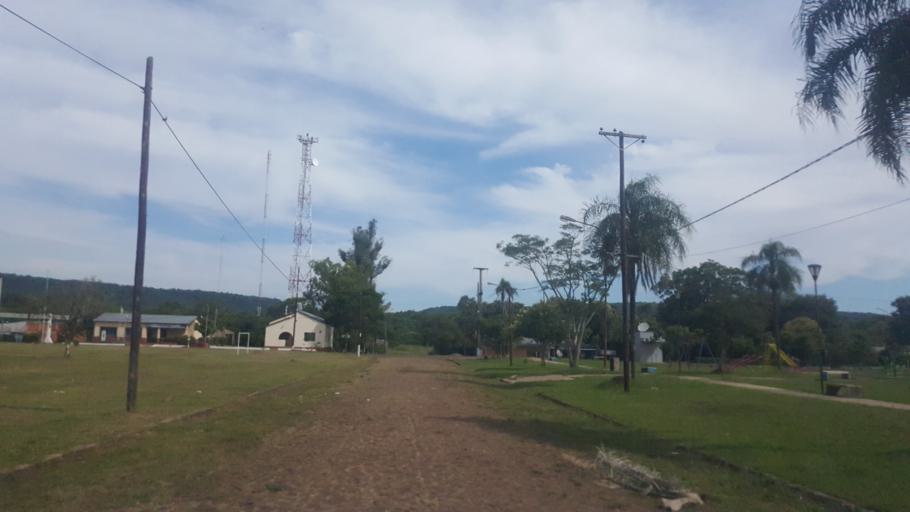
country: AR
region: Misiones
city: Cerro Cora
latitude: -27.5114
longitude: -55.6093
